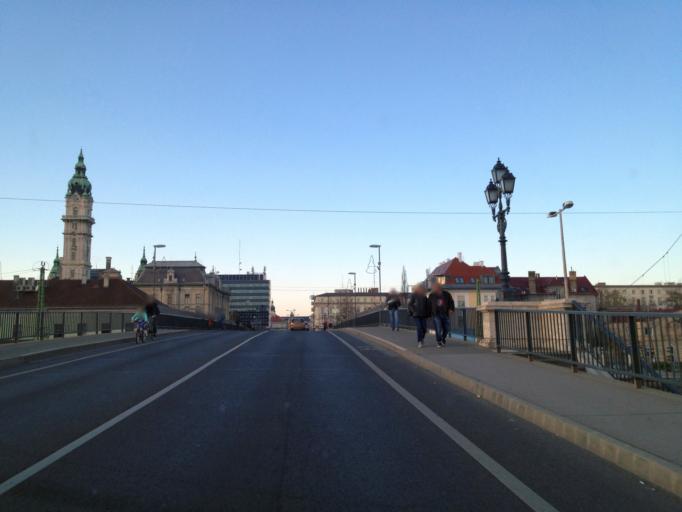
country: HU
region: Gyor-Moson-Sopron
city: Gyor
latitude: 47.6820
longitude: 17.6371
